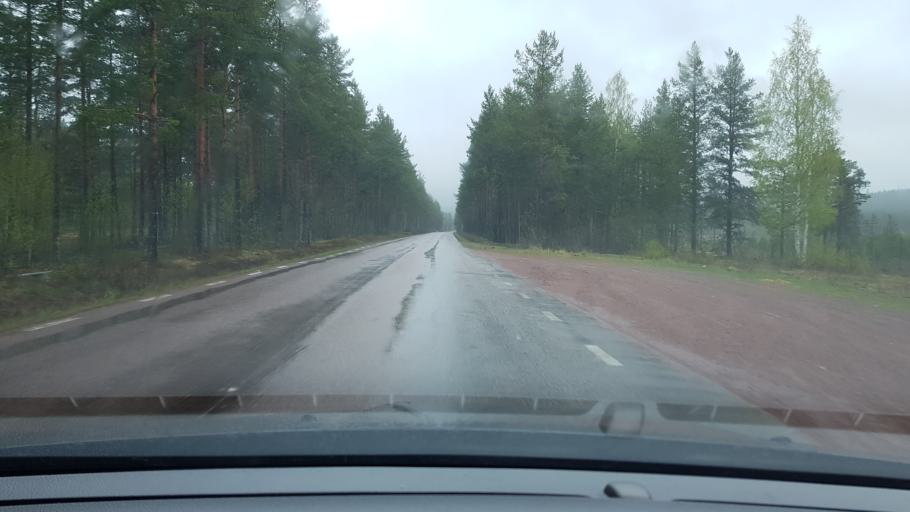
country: SE
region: Dalarna
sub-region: Alvdalens Kommun
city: AElvdalen
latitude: 61.1249
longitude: 14.1734
